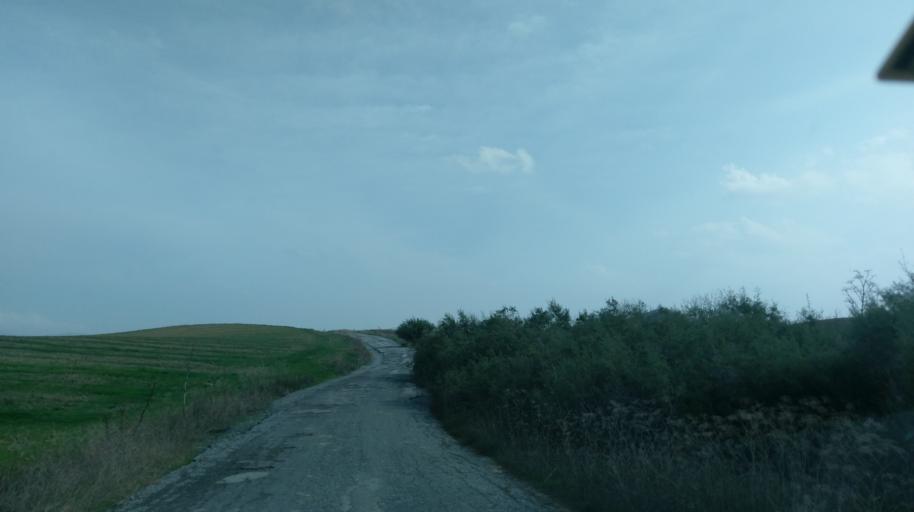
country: CY
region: Keryneia
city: Lapithos
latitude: 35.2622
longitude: 33.1010
